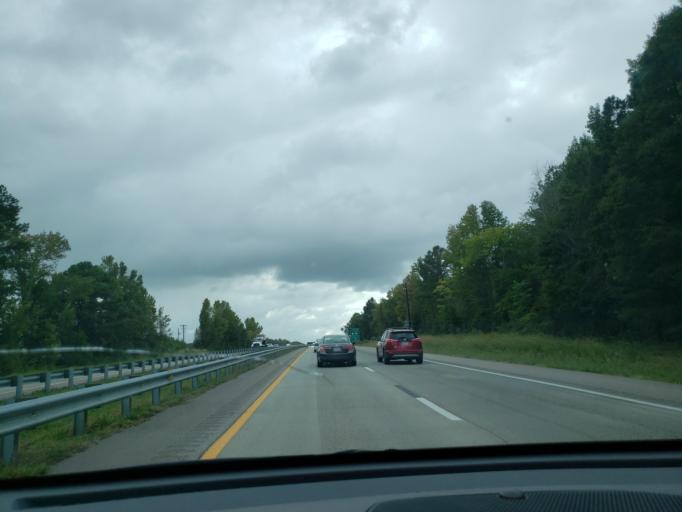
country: US
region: Virginia
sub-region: Mecklenburg County
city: Bracey
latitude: 36.5400
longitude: -78.1871
